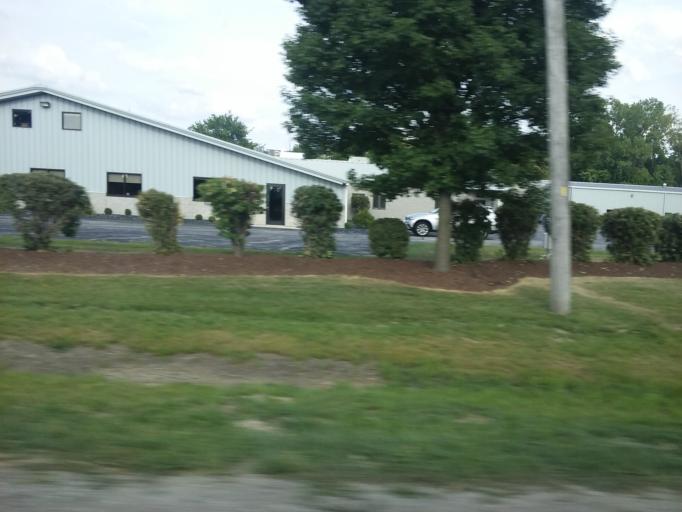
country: US
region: Ohio
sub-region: Wood County
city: Bowling Green
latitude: 41.3388
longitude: -83.6501
